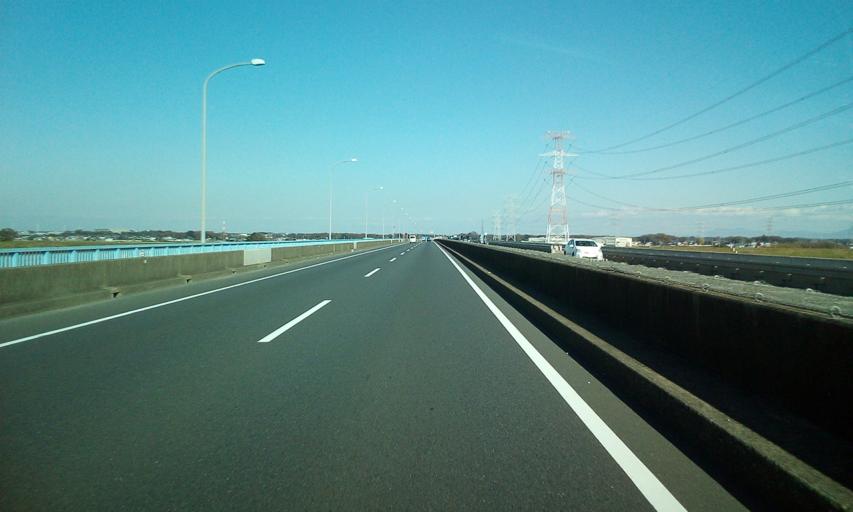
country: JP
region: Ibaraki
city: Sakai
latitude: 36.1255
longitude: 139.7572
